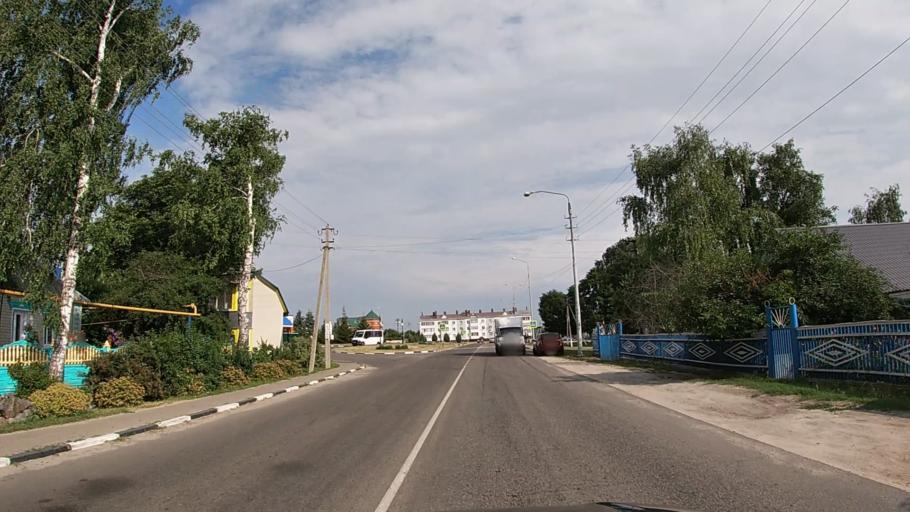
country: RU
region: Belgorod
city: Krasnaya Yaruga
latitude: 50.8011
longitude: 35.6604
